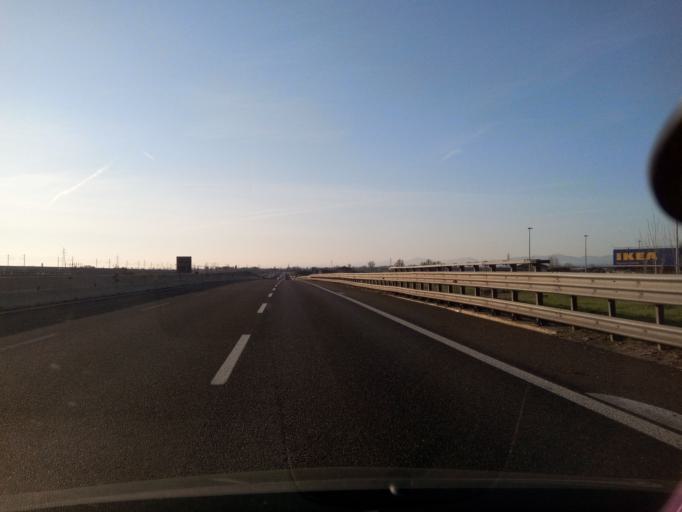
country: IT
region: Emilia-Romagna
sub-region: Provincia di Piacenza
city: Pontenure
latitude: 45.0329
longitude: 9.7664
